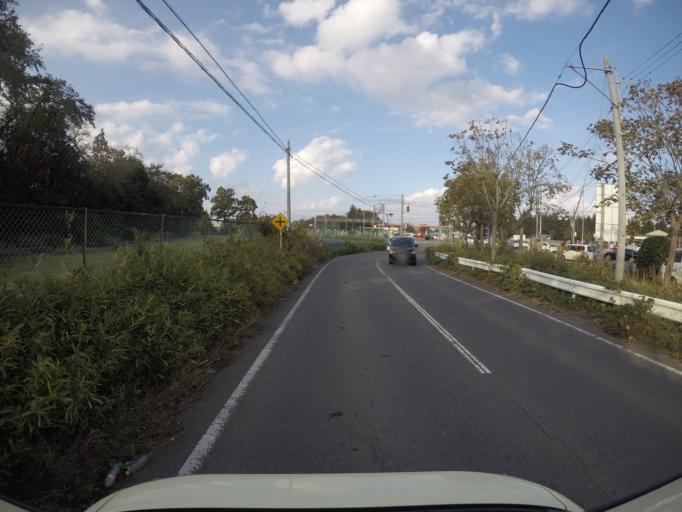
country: JP
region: Ibaraki
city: Naka
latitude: 36.0530
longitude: 140.0844
